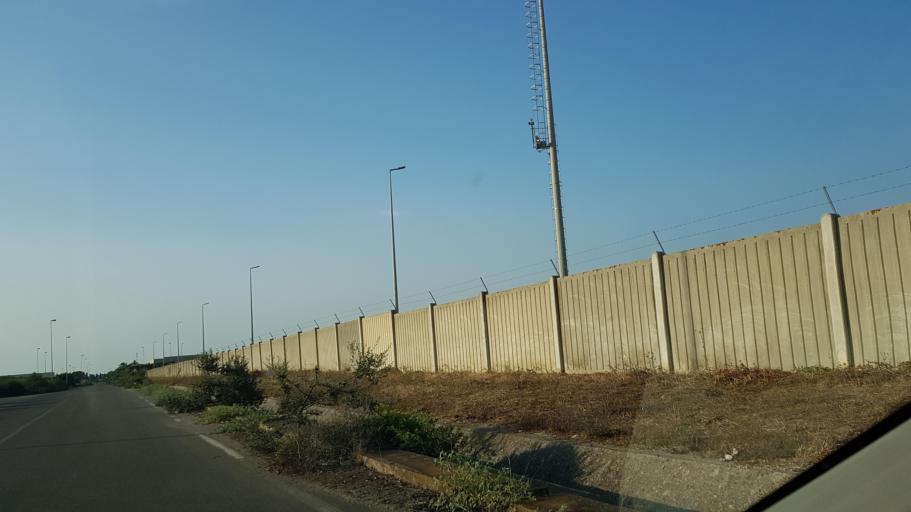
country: IT
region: Apulia
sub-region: Provincia di Brindisi
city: La Rosa
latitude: 40.6222
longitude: 17.9750
